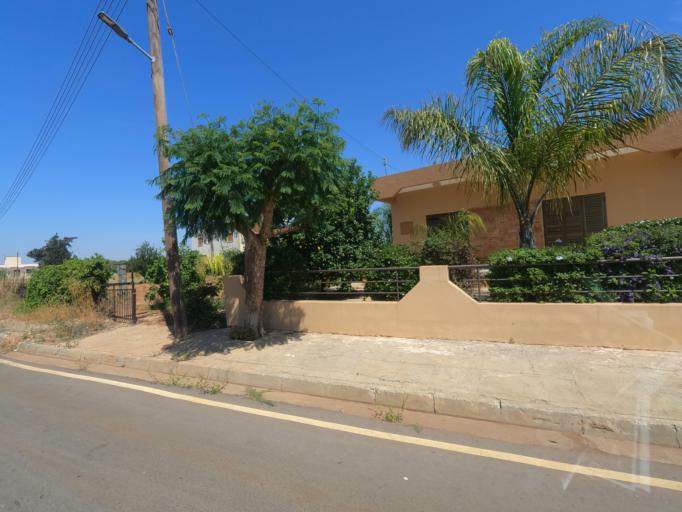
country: CY
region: Ammochostos
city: Liopetri
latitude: 35.0144
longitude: 33.8902
